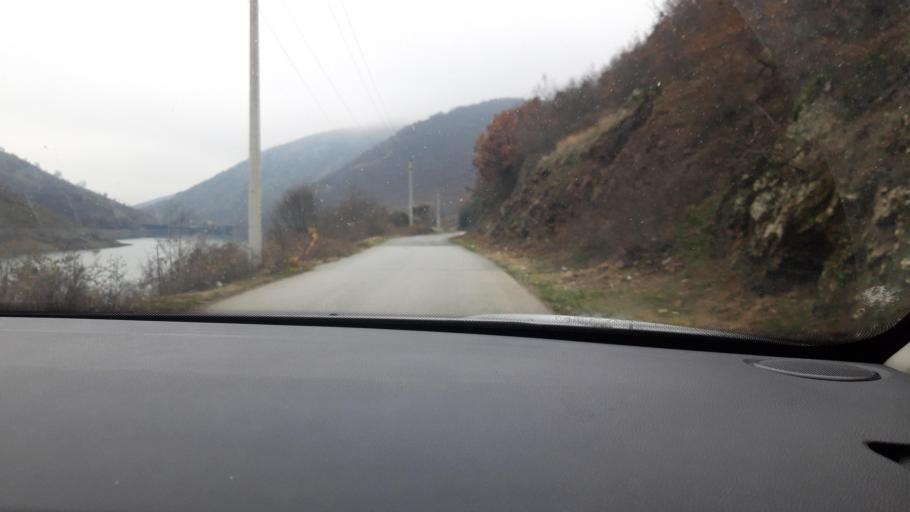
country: MK
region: Opstina Lipkovo
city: Lipkovo
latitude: 42.1721
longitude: 21.5694
